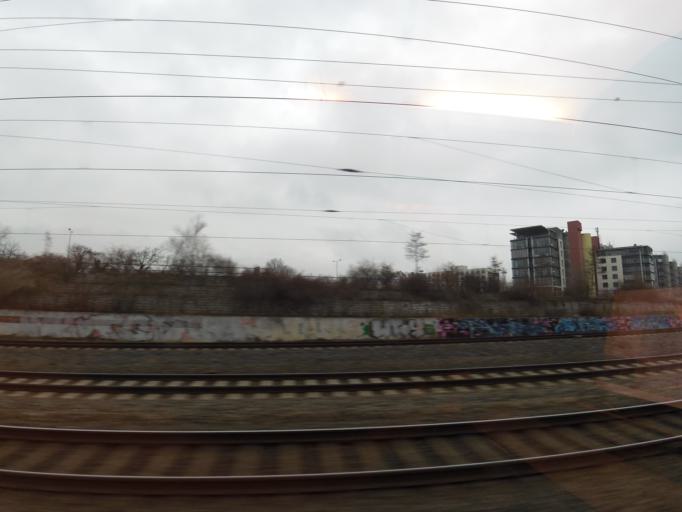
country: DE
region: Saxony
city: Leipzig
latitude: 51.3630
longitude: 12.4009
